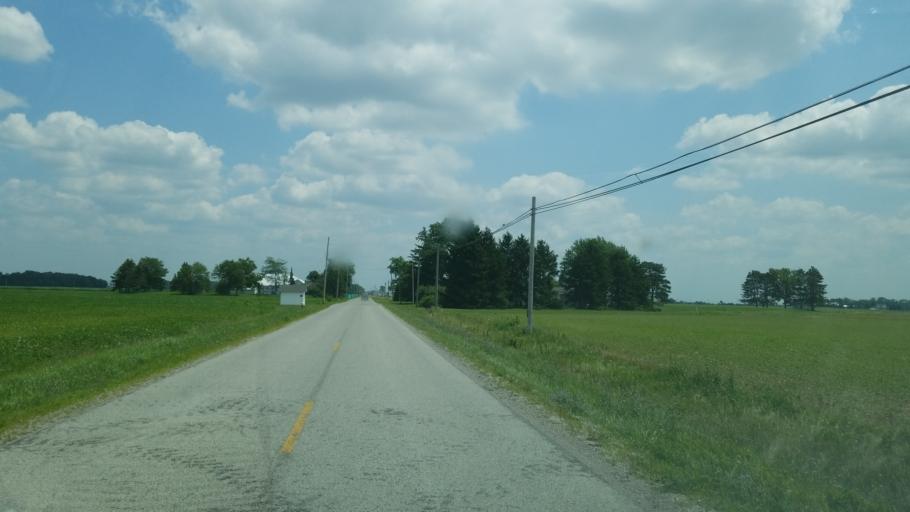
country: US
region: Ohio
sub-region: Henry County
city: Napoleon
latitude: 41.3417
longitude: -84.0492
